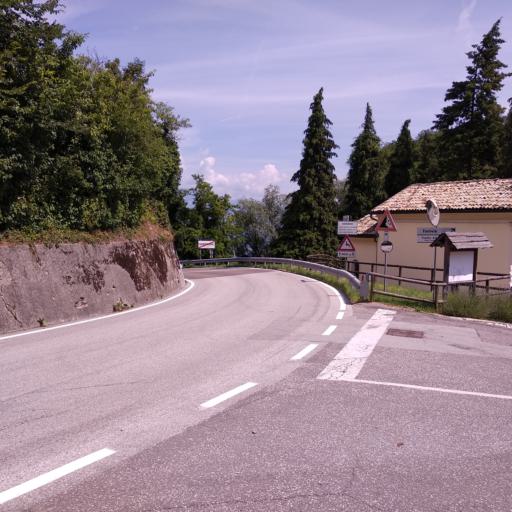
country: IT
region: Trentino-Alto Adige
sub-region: Provincia di Trento
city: Trento
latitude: 46.0653
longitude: 11.0988
